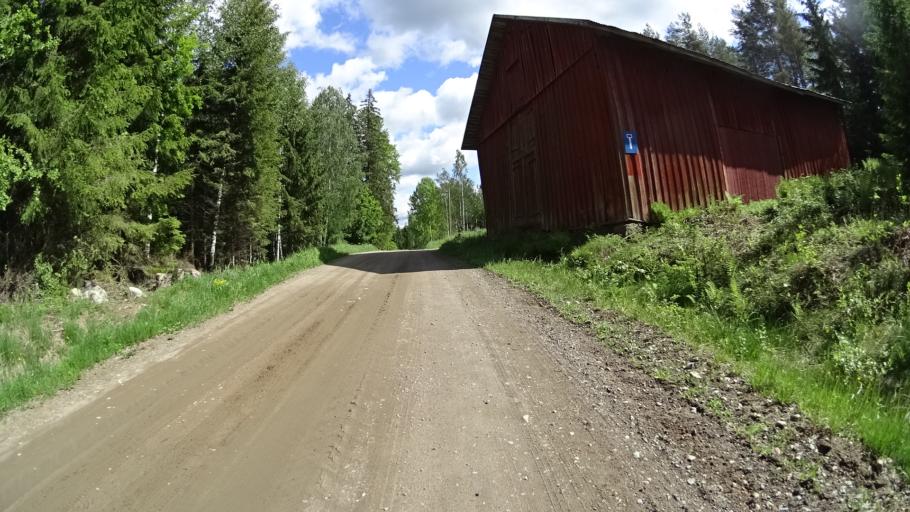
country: FI
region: Uusimaa
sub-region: Raaseporin
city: Pohja
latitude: 60.1214
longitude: 23.5901
